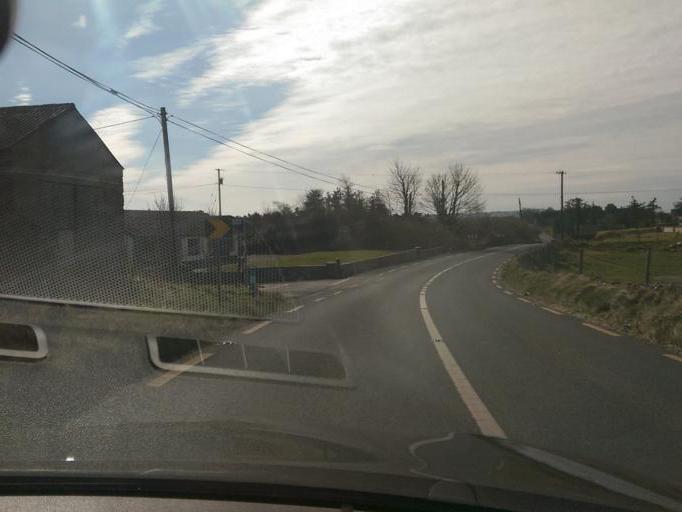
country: IE
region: Connaught
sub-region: County Galway
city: Athenry
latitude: 53.4623
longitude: -8.6710
